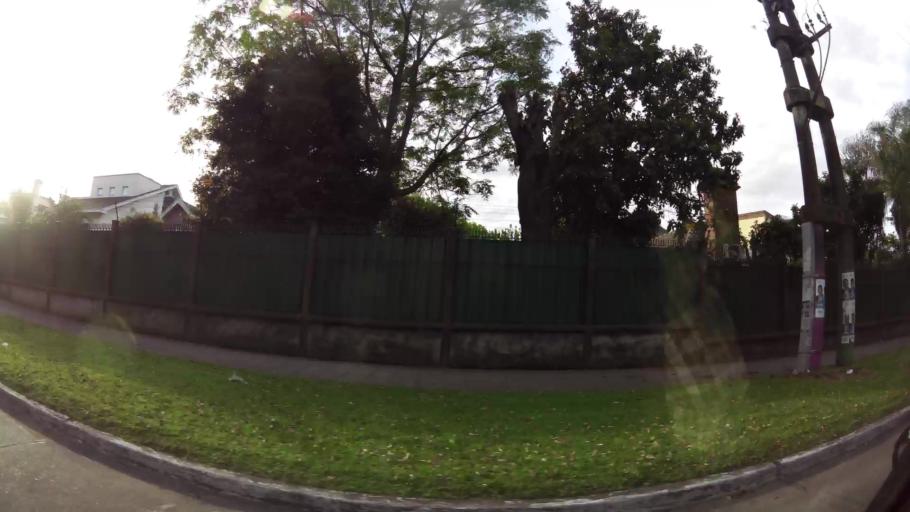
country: AR
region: Buenos Aires
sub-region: Partido de Quilmes
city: Quilmes
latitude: -34.7241
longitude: -58.2427
